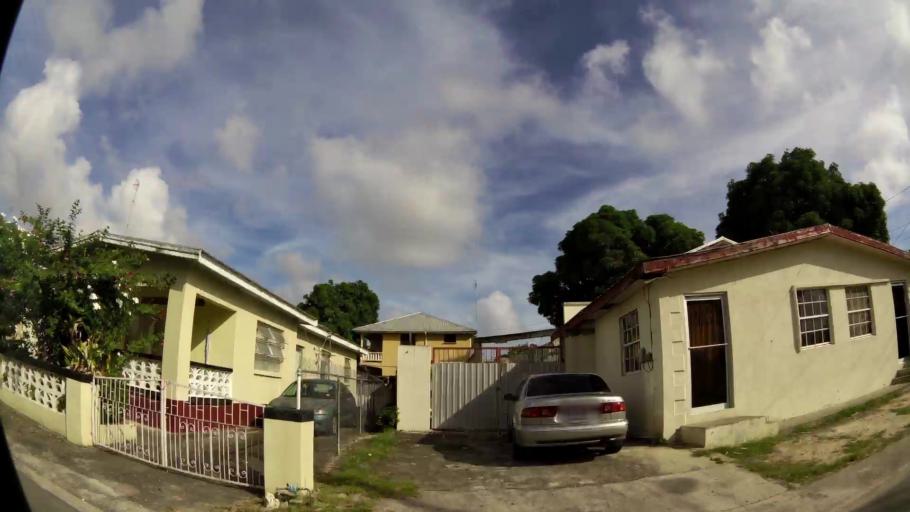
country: BB
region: Saint Michael
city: Bridgetown
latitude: 13.0850
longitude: -59.5922
